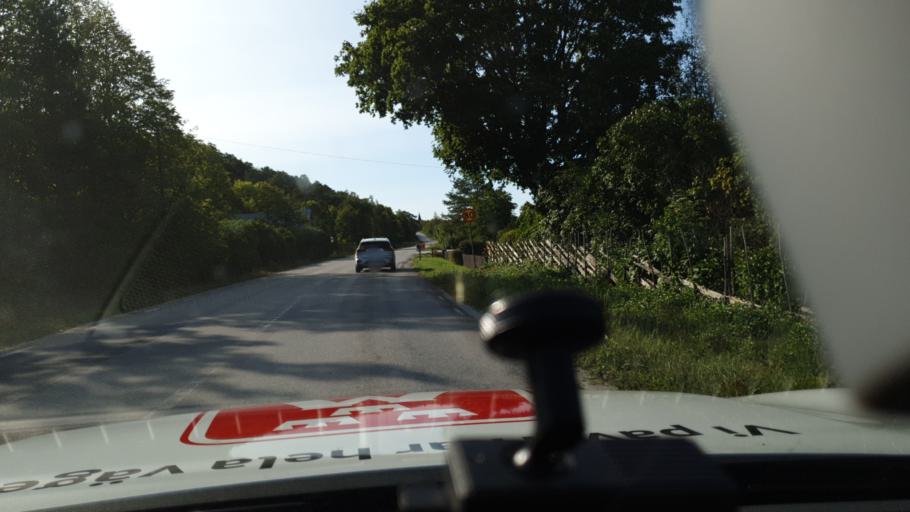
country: SE
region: Gotland
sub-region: Gotland
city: Klintehamn
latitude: 57.3454
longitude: 18.1922
